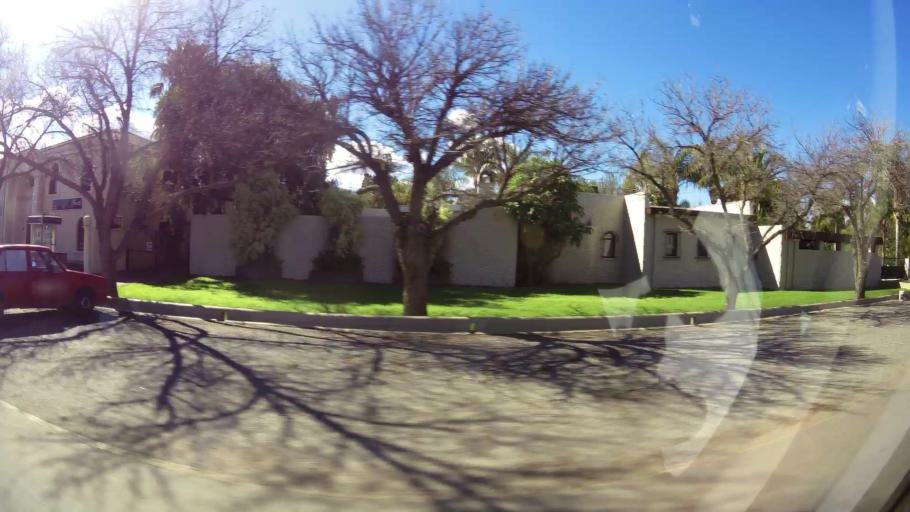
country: ZA
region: Western Cape
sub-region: Cape Winelands District Municipality
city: Ashton
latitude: -33.8105
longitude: 19.8893
